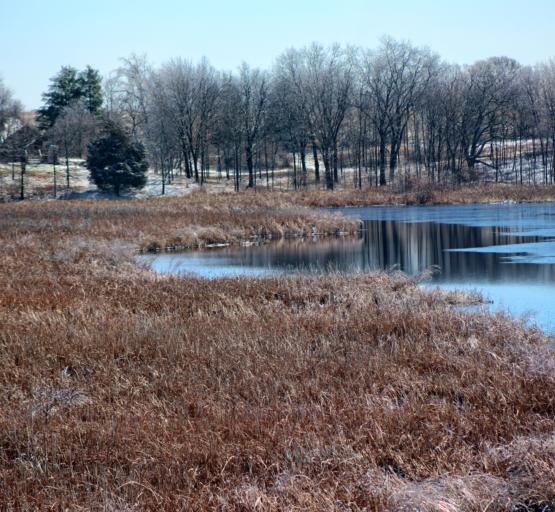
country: US
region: Wisconsin
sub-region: Jefferson County
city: Lake Ripley
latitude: 42.9809
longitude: -88.9798
